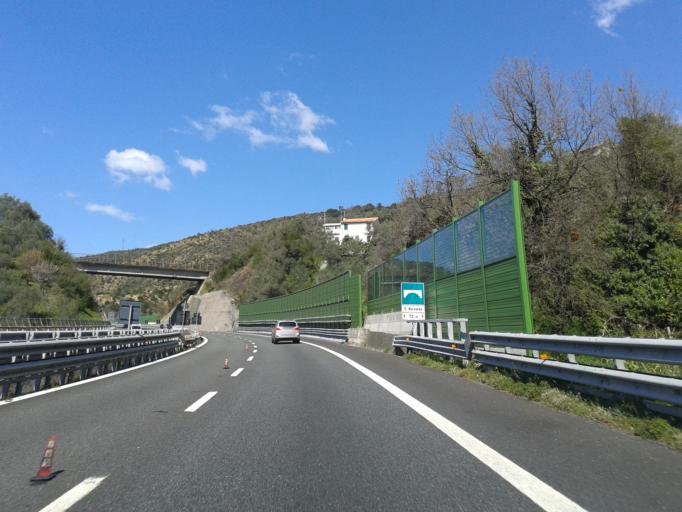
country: IT
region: Liguria
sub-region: Provincia di Genova
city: Sestri Levante
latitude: 44.2833
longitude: 9.4085
